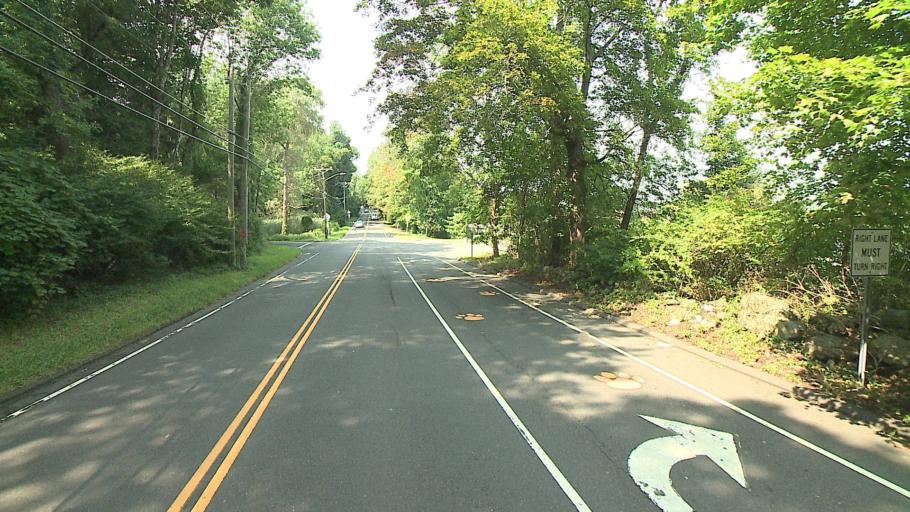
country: US
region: Connecticut
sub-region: Fairfield County
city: Ridgefield
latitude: 41.3256
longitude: -73.5321
